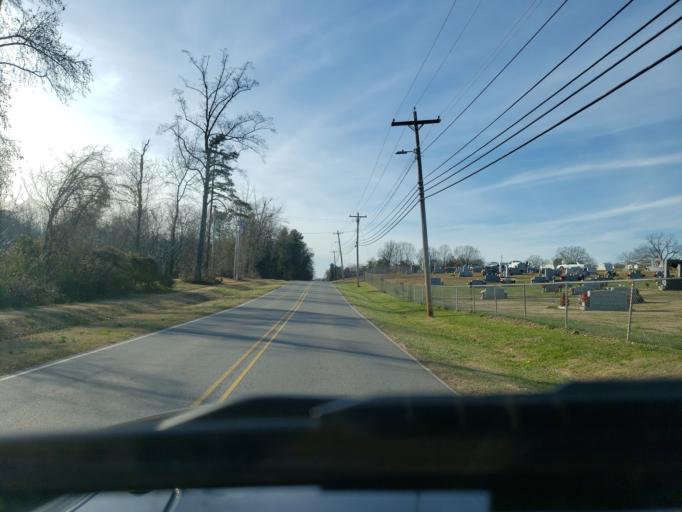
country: US
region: North Carolina
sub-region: Cleveland County
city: Kings Mountain
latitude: 35.2376
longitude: -81.3352
